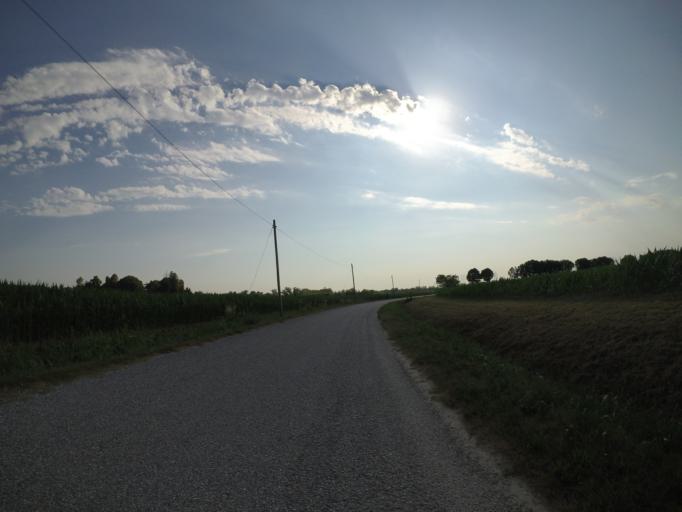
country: IT
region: Friuli Venezia Giulia
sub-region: Provincia di Udine
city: Camino al Tagliamento
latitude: 45.9511
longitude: 12.9206
